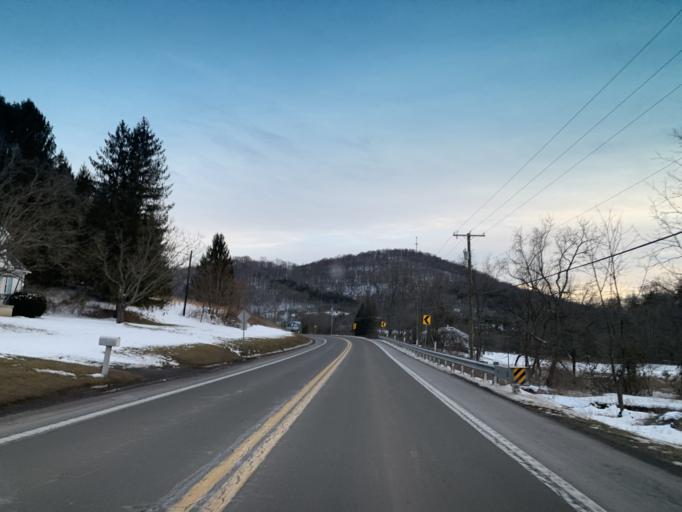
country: US
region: Maryland
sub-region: Allegany County
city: Cumberland
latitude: 39.7284
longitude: -78.7120
